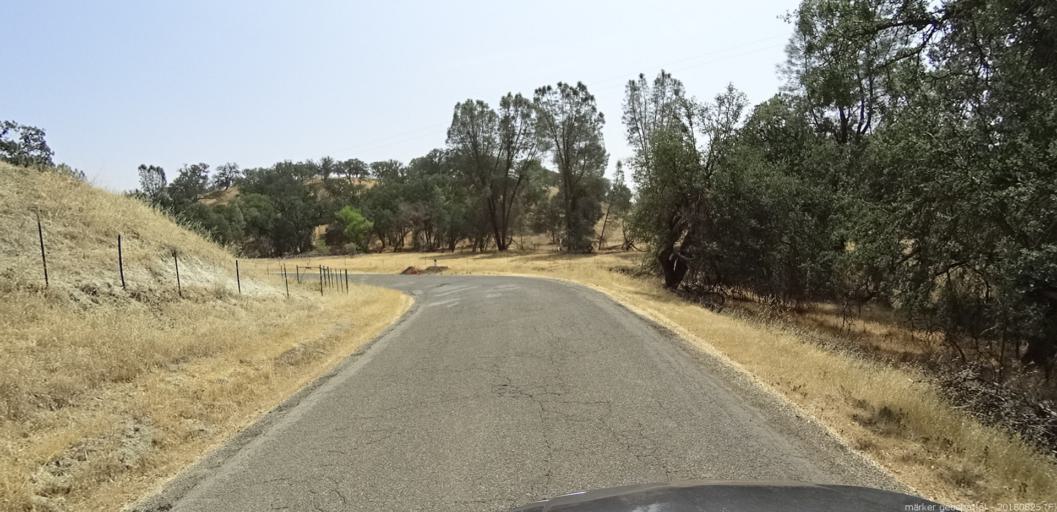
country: US
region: California
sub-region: San Luis Obispo County
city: Shandon
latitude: 35.8766
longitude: -120.4143
